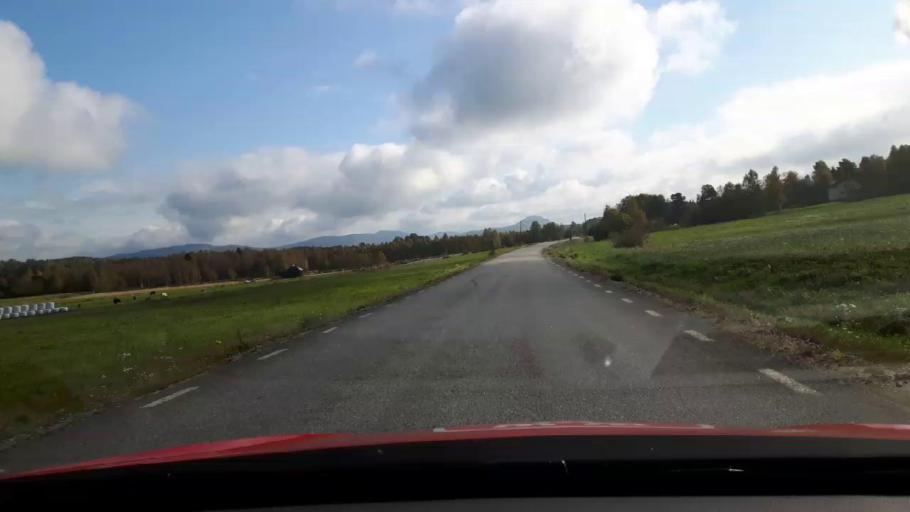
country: SE
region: Gaevleborg
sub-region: Ljusdals Kommun
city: Ljusdal
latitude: 61.7605
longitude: 16.0895
